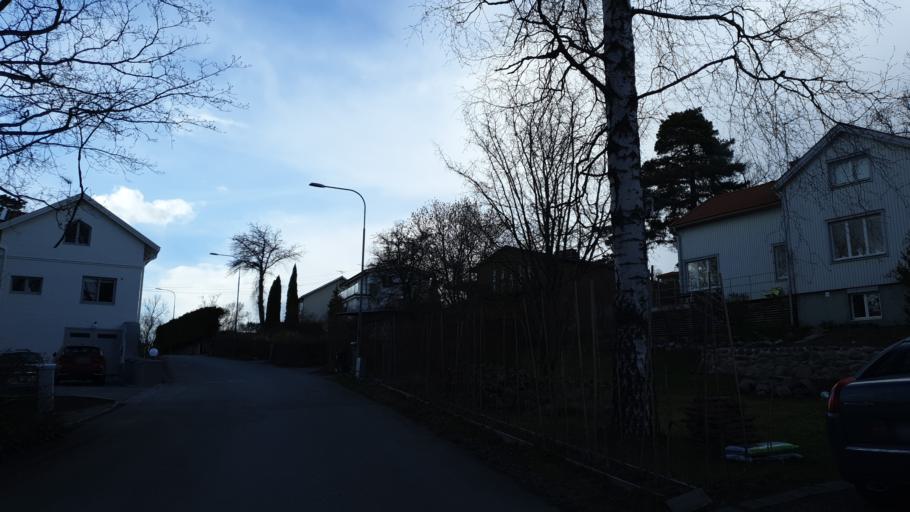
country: SE
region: Stockholm
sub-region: Lidingo
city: Lidingoe
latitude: 59.3718
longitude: 18.1181
